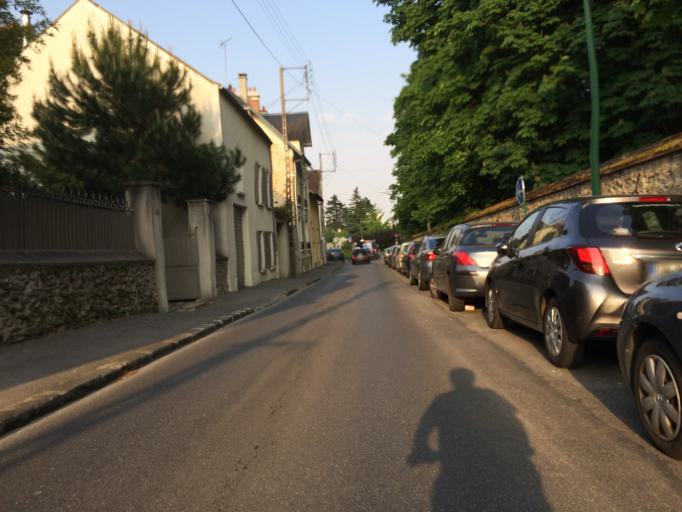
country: FR
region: Ile-de-France
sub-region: Departement de l'Essonne
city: Igny
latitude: 48.7393
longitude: 2.2461
